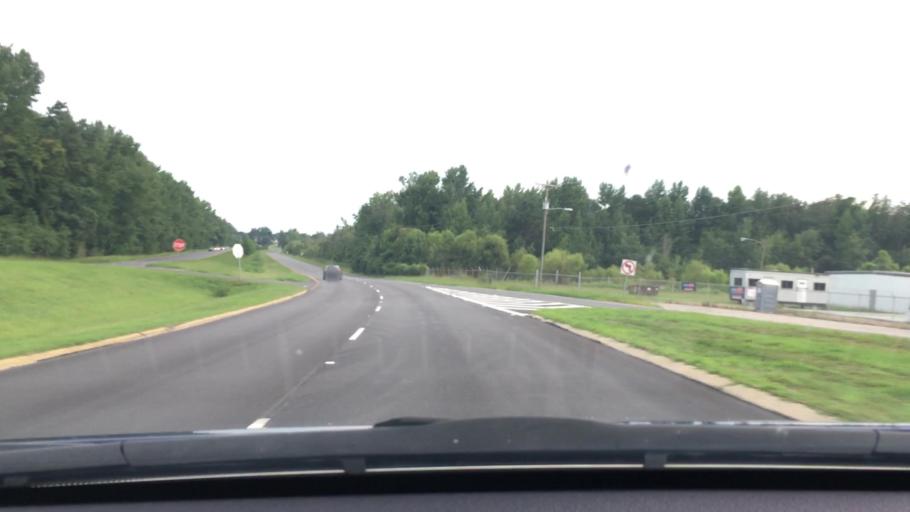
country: US
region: South Carolina
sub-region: Sumter County
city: South Sumter
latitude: 33.8813
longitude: -80.3511
